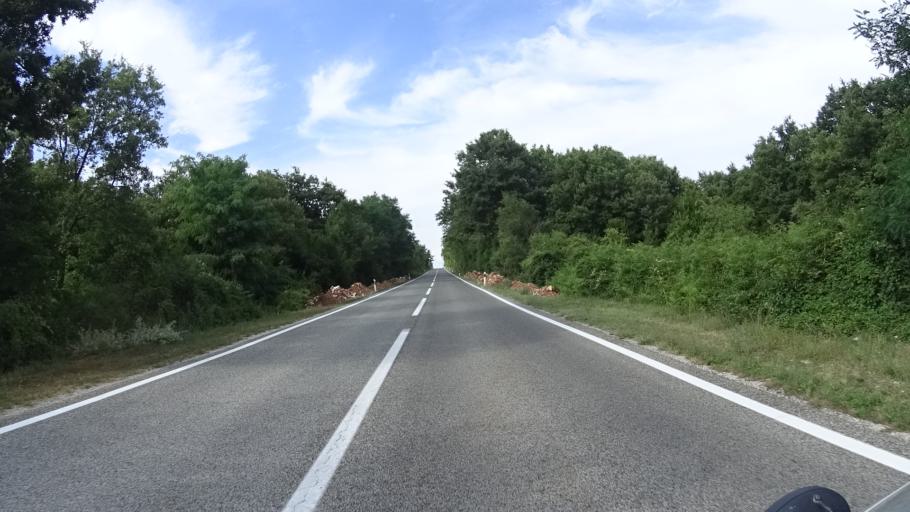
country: HR
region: Istarska
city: Marcana
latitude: 45.0252
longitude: 13.9918
